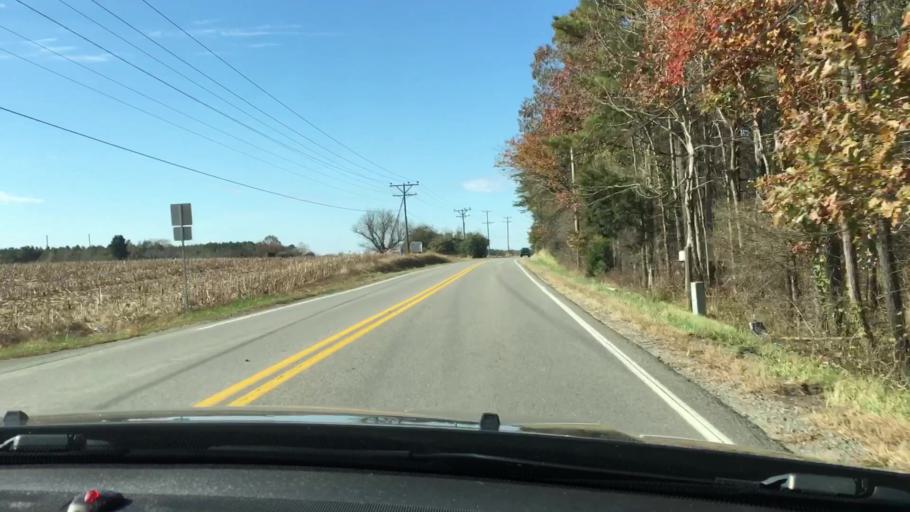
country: US
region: Virginia
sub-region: King William County
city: Central Garage
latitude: 37.7225
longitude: -77.0853
